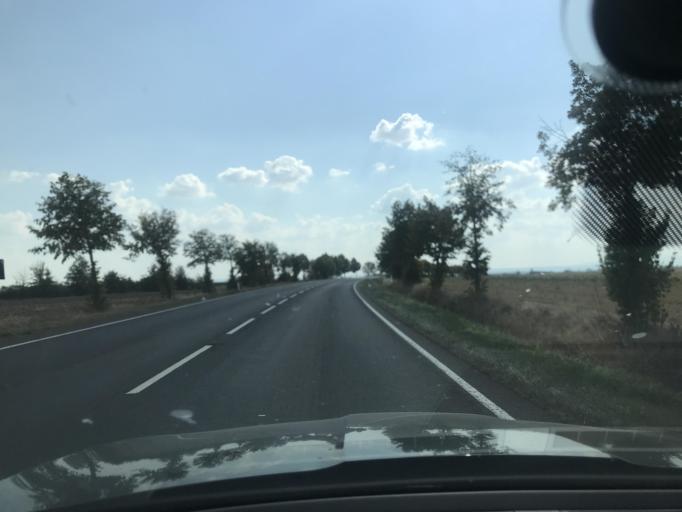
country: DE
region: Saxony-Anhalt
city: Groeningen
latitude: 51.9326
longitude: 11.1834
